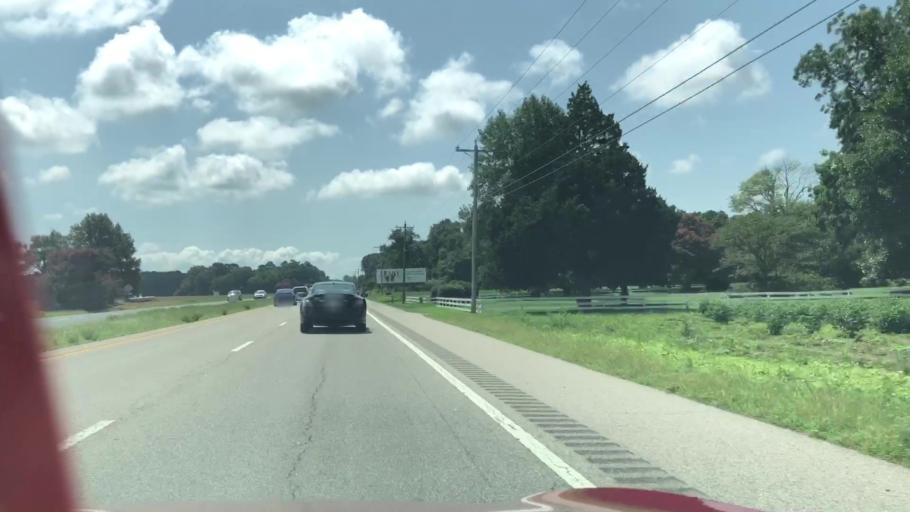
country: US
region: Virginia
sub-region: Northampton County
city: Cape Charles
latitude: 37.2414
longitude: -75.9715
